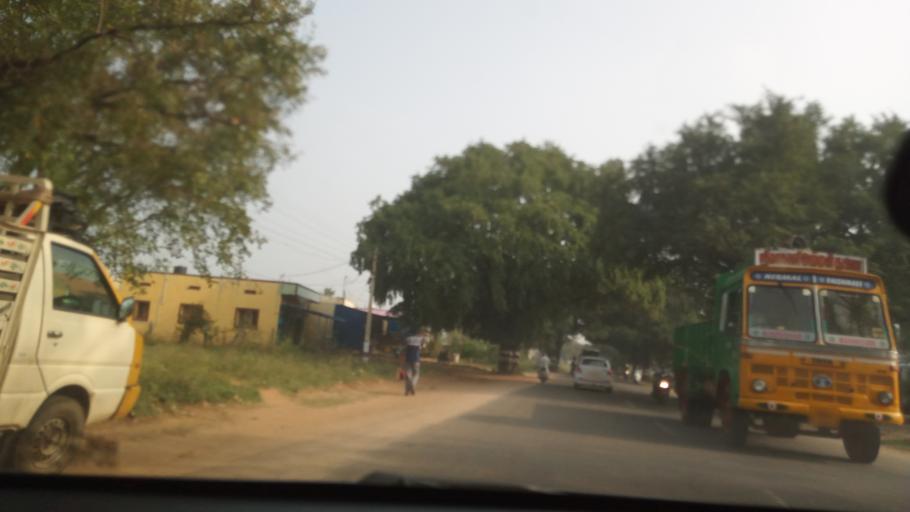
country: IN
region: Tamil Nadu
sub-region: Coimbatore
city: Annur
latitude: 11.1769
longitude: 77.0584
